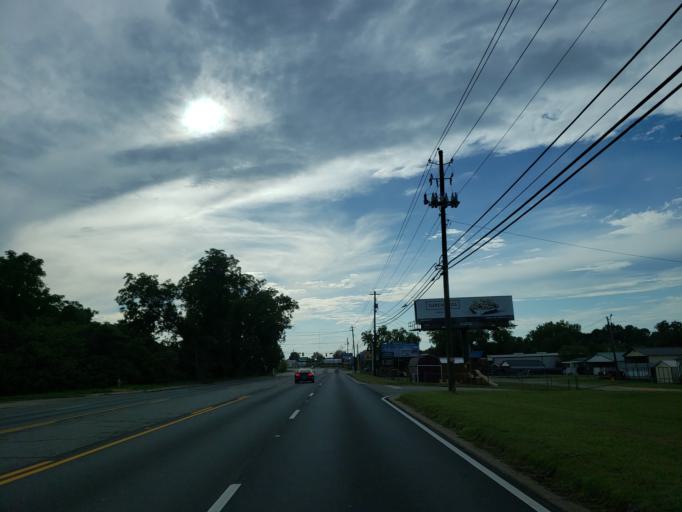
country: US
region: Georgia
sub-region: Tift County
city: Tifton
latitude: 31.4490
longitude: -83.4941
